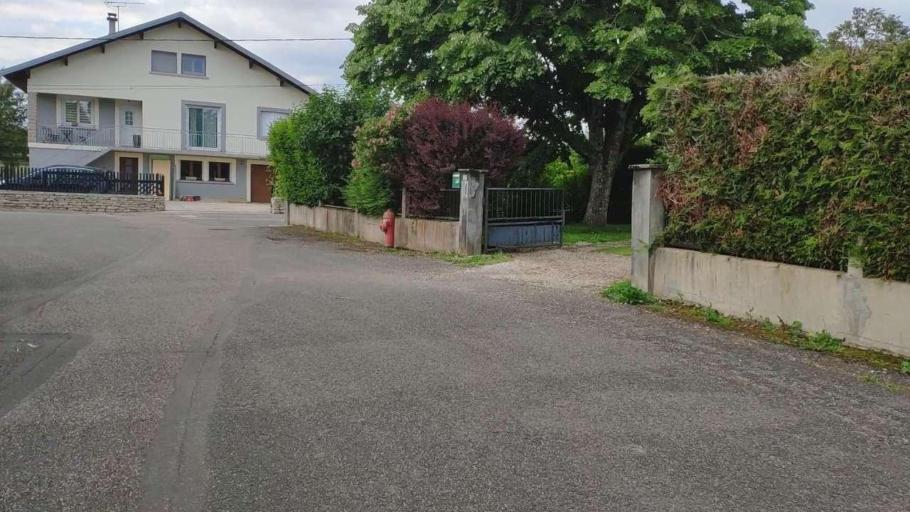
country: FR
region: Franche-Comte
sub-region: Departement du Jura
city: Perrigny
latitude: 46.7620
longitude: 5.5947
